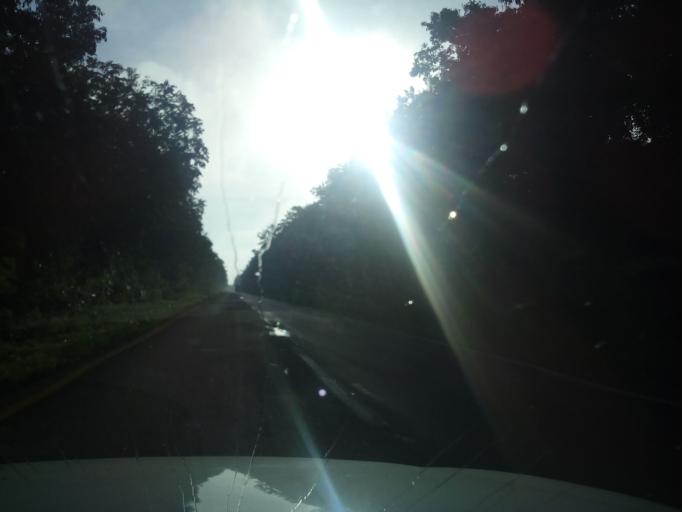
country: MX
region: Yucatan
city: Tunkas
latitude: 20.7665
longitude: -88.8097
